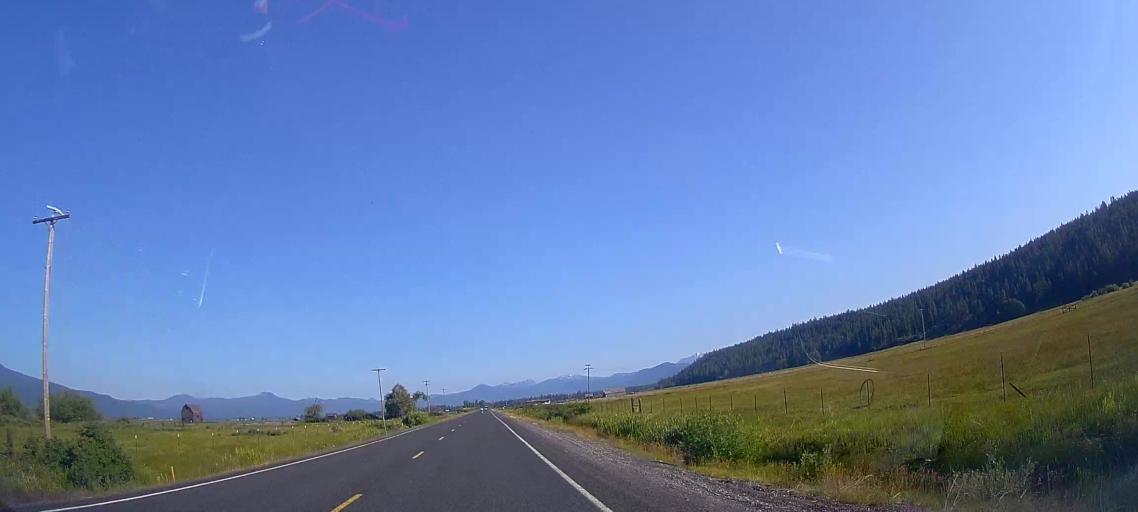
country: US
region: Oregon
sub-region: Klamath County
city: Klamath Falls
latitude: 42.6487
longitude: -121.9547
